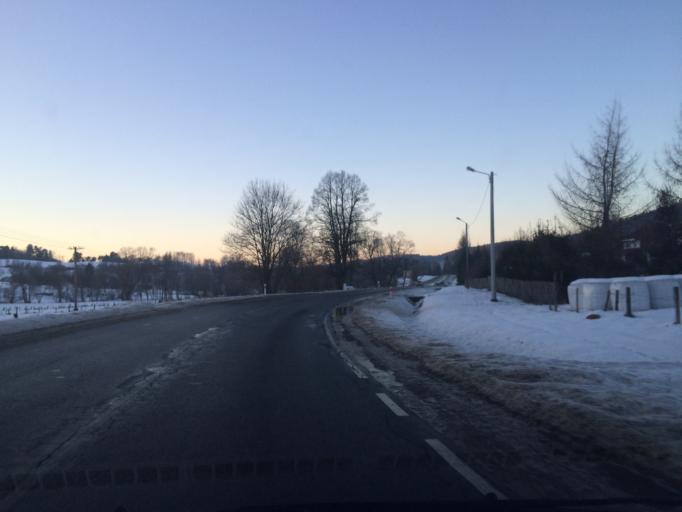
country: PL
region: Subcarpathian Voivodeship
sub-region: Powiat bieszczadzki
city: Czarna
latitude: 49.3734
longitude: 22.6468
